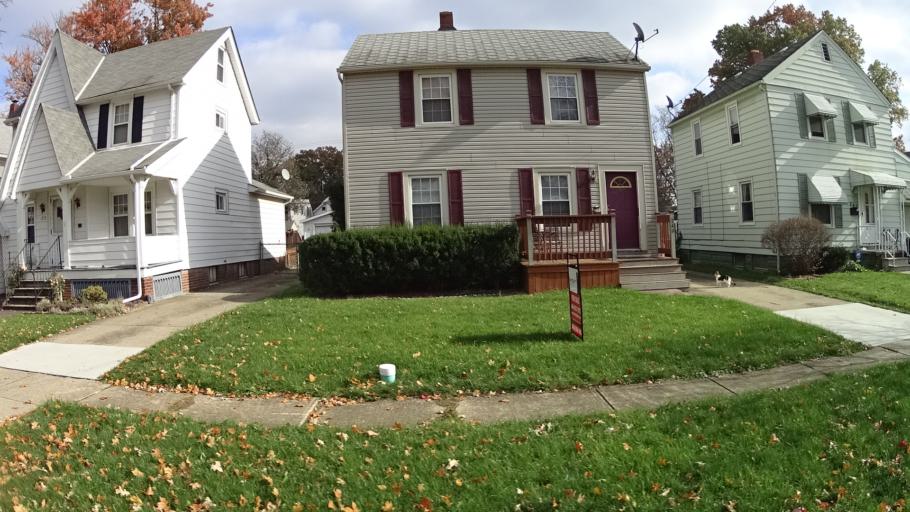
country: US
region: Ohio
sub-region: Lorain County
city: Elyria
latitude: 41.3796
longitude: -82.0882
